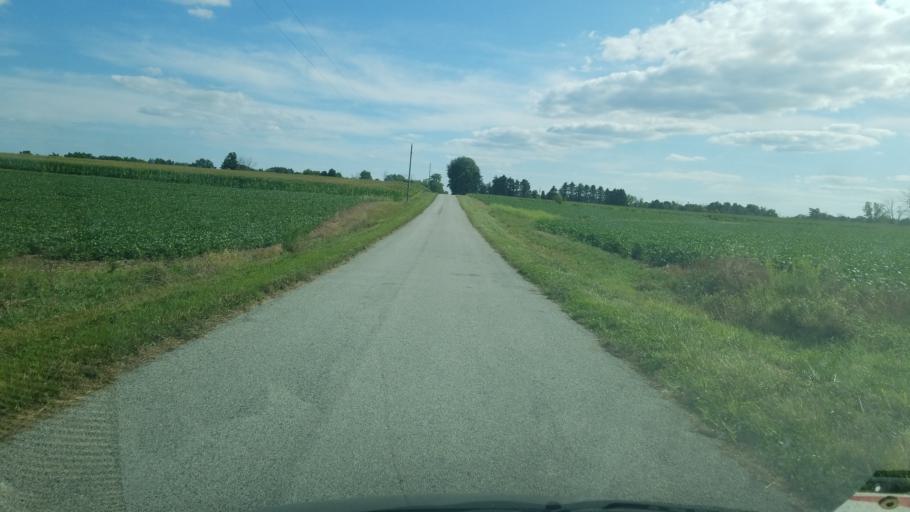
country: US
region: Ohio
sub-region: Champaign County
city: Saint Paris
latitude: 40.1437
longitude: -83.8722
